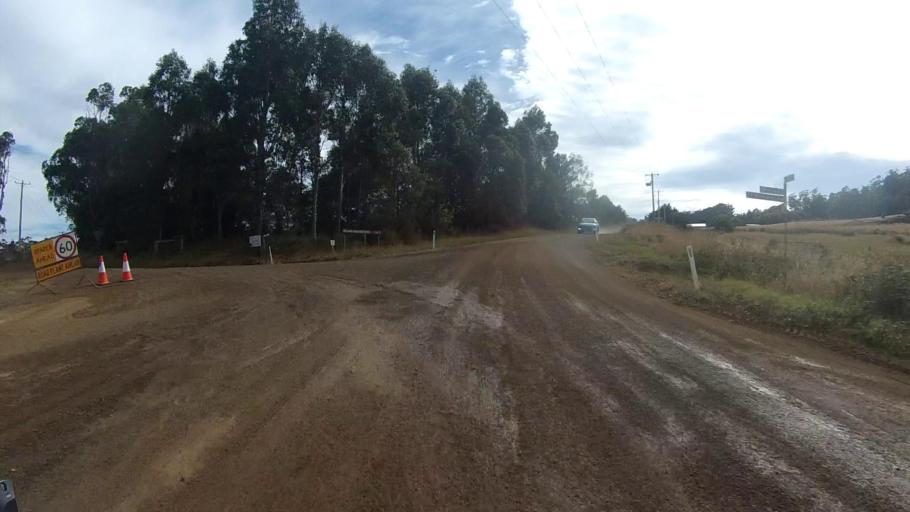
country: AU
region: Tasmania
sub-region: Sorell
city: Sorell
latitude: -42.7808
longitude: 147.8103
